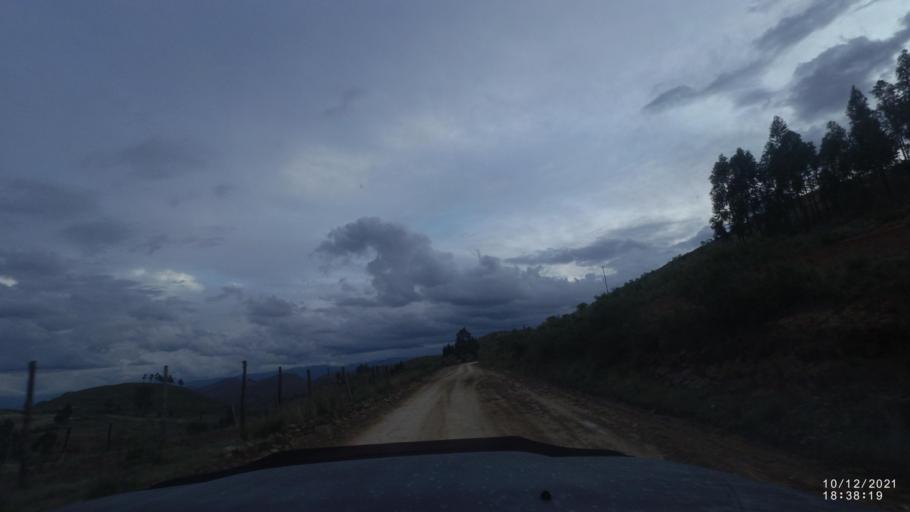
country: BO
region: Cochabamba
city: Tarata
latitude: -17.8412
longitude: -65.9889
